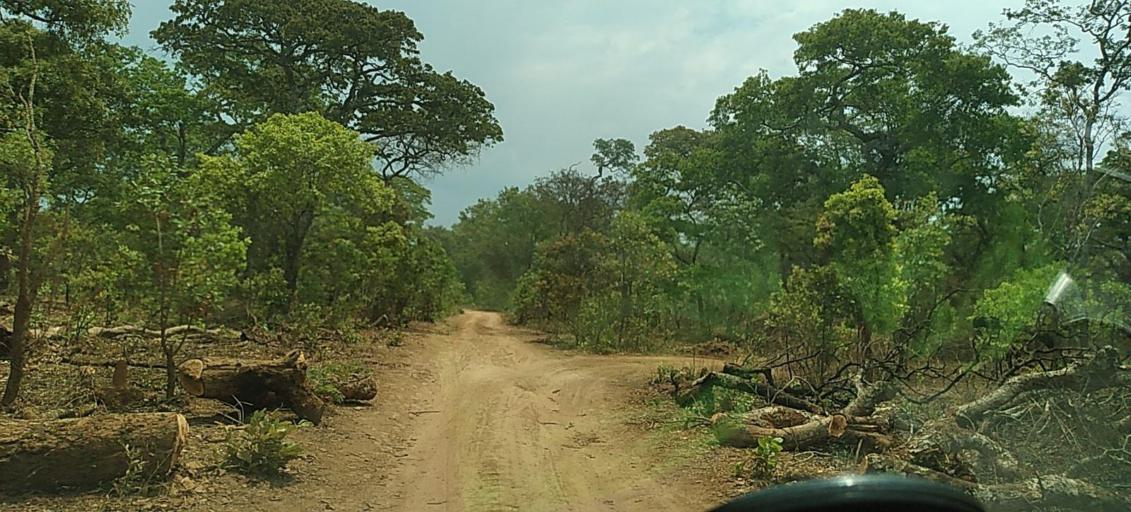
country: ZM
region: North-Western
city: Kansanshi
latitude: -12.0111
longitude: 26.2581
